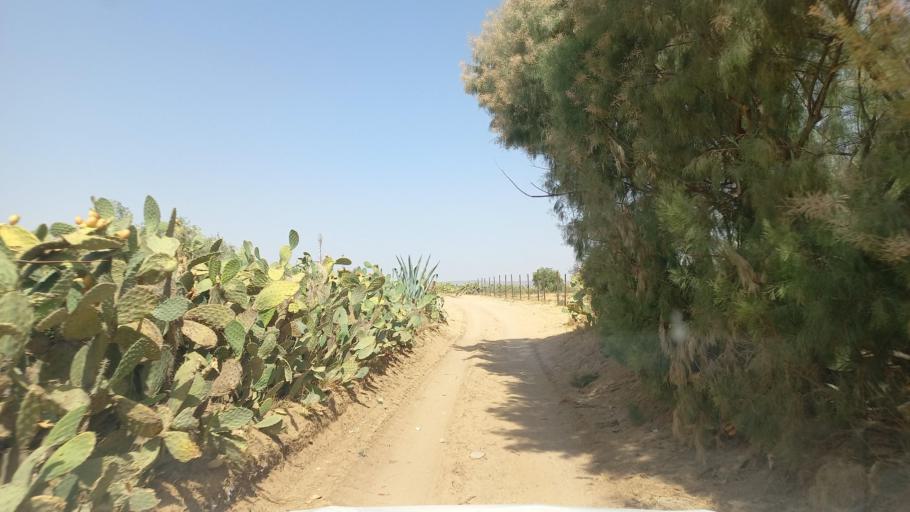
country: TN
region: Al Qasrayn
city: Kasserine
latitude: 35.2506
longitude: 9.0307
